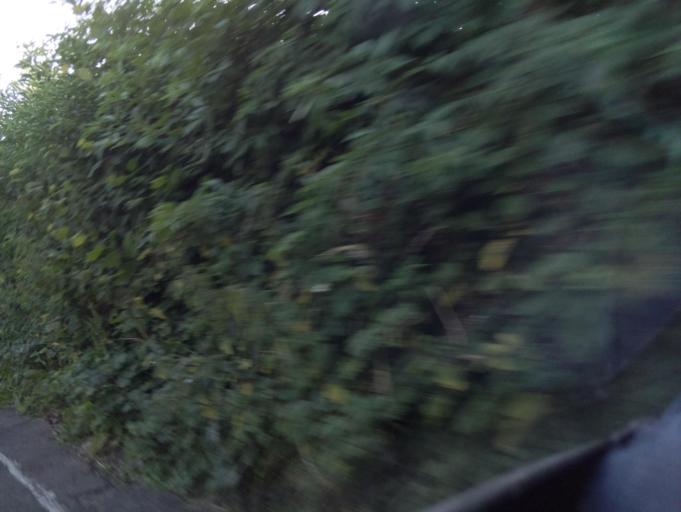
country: GB
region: England
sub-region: South Gloucestershire
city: Marshfield
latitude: 51.4873
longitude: -2.3116
